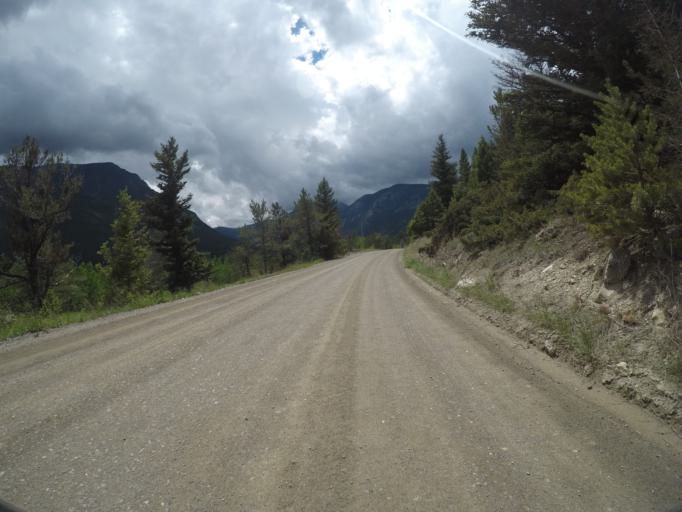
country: US
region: Montana
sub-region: Park County
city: Livingston
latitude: 45.5333
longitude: -110.2125
